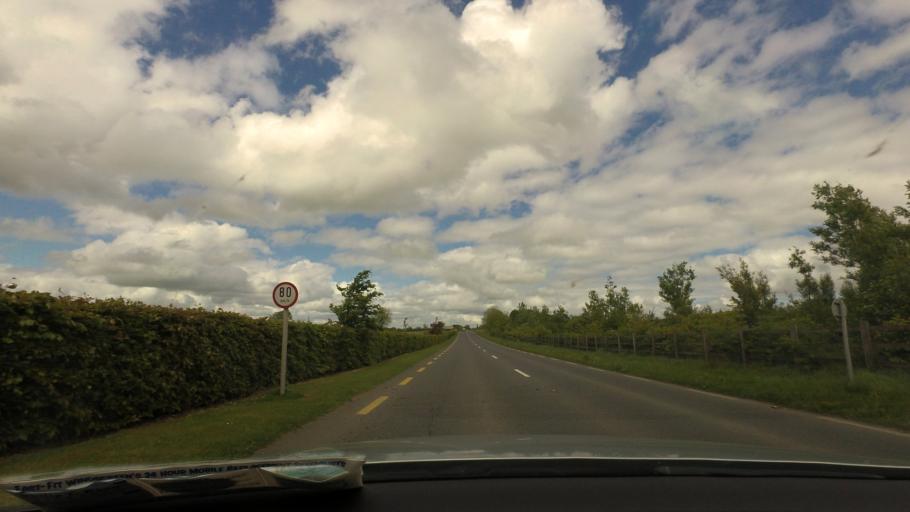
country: IE
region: Munster
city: Cashel
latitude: 52.5452
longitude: -7.8655
